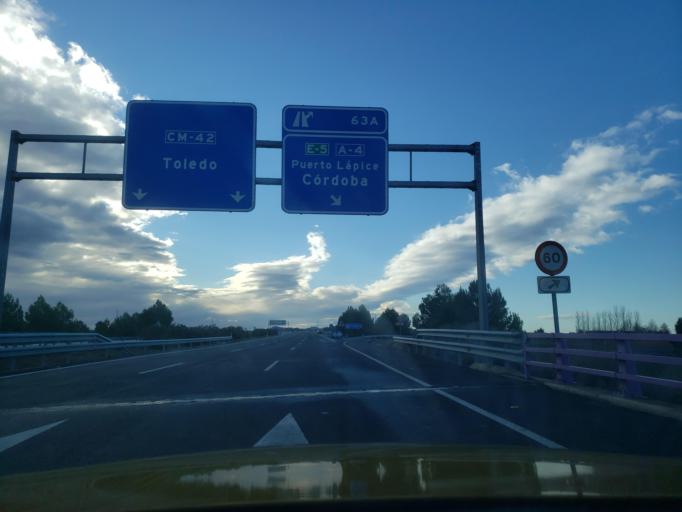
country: ES
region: Castille-La Mancha
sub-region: Province of Toledo
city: Madridejos
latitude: 39.4472
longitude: -3.5268
